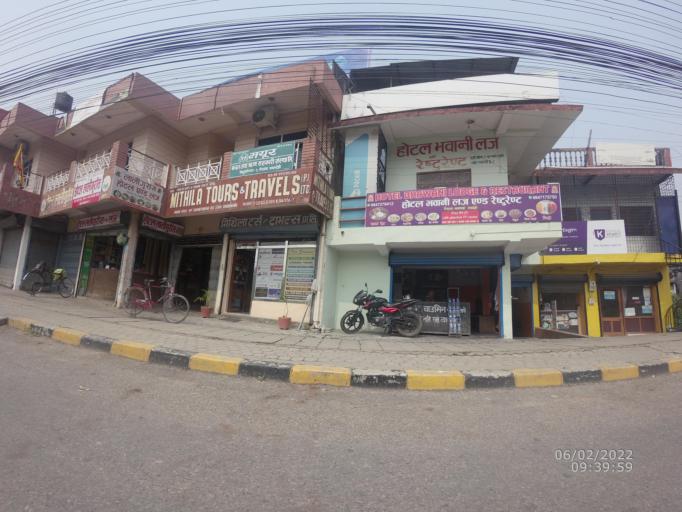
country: NP
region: Western Region
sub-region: Lumbini Zone
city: Bhairahawa
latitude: 27.5004
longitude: 83.4577
